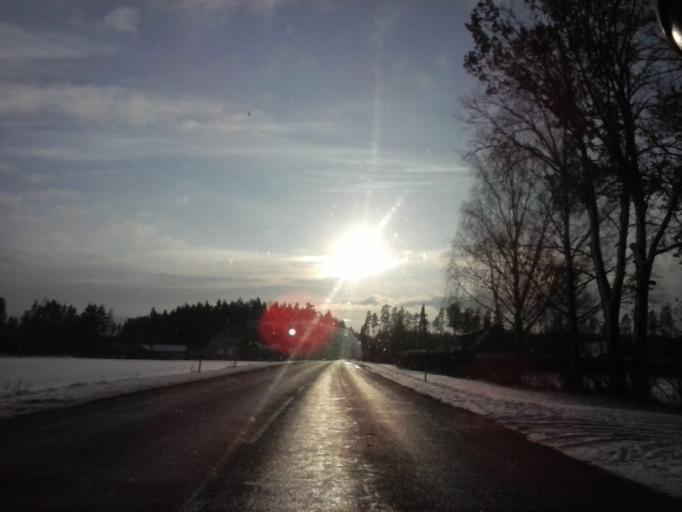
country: EE
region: Tartu
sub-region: UElenurme vald
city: Ulenurme
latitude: 58.3453
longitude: 26.9110
